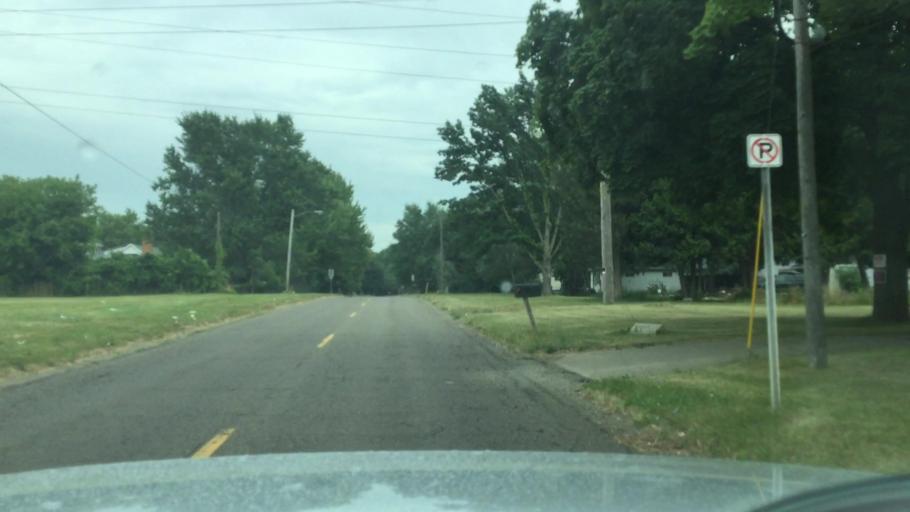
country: US
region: Michigan
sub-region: Genesee County
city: Beecher
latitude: 43.0686
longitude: -83.6714
